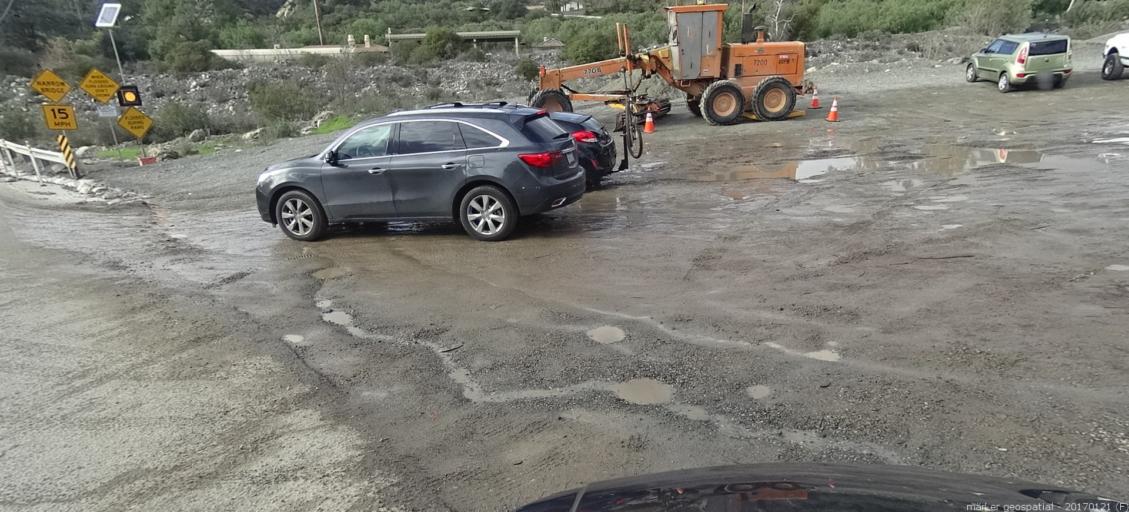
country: US
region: California
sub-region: Orange County
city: Trabuco Canyon
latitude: 33.6591
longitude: -117.5855
